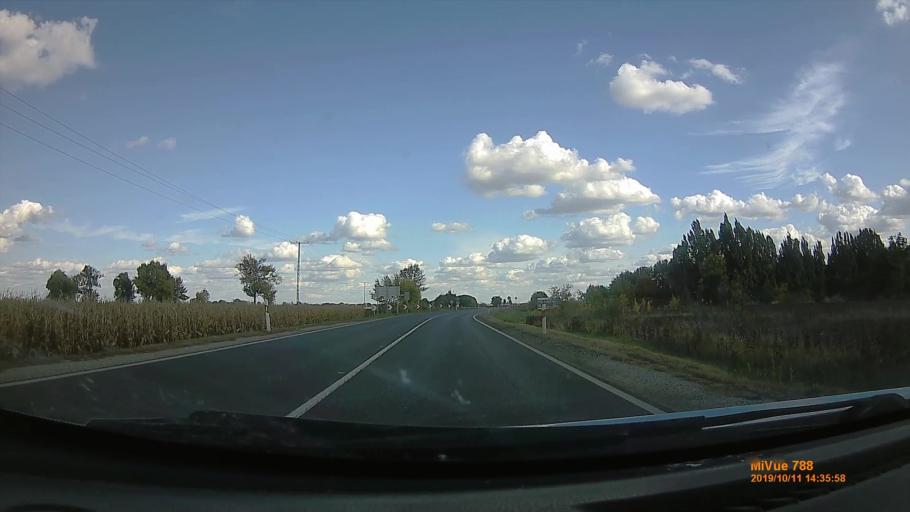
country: HU
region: Hajdu-Bihar
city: Ebes
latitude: 47.5586
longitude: 21.5009
